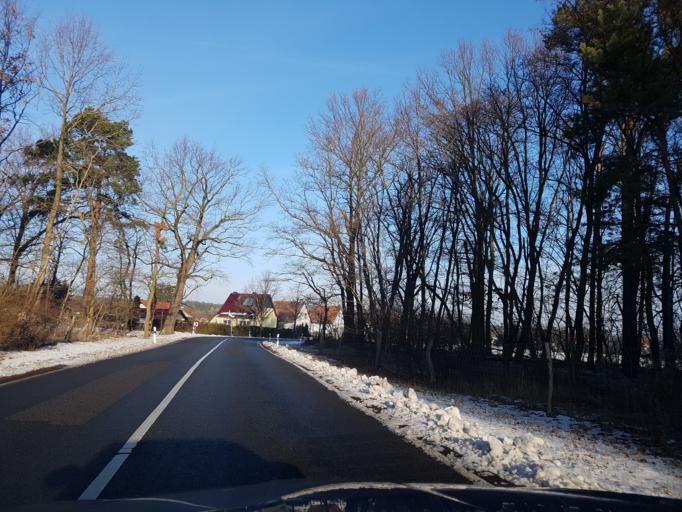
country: DE
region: Brandenburg
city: Bad Liebenwerda
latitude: 51.5331
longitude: 13.4099
